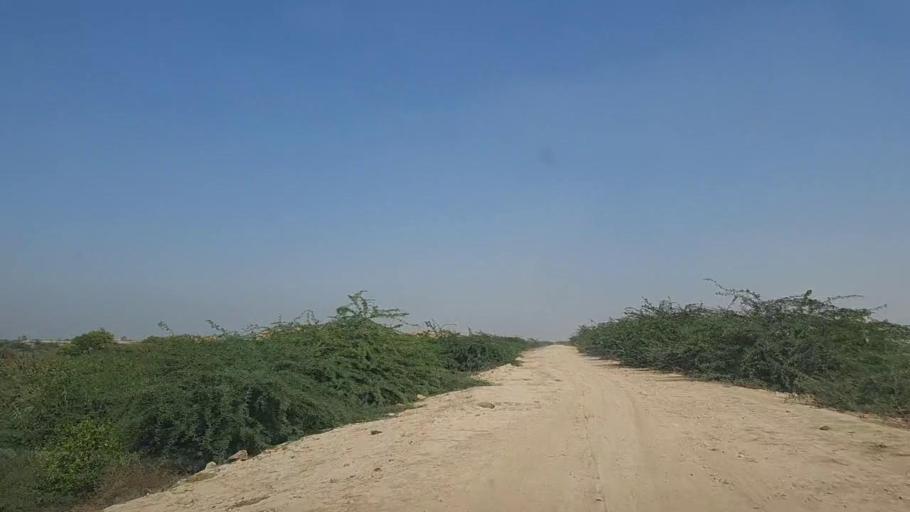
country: PK
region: Sindh
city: Daro Mehar
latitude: 24.8631
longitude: 68.0410
